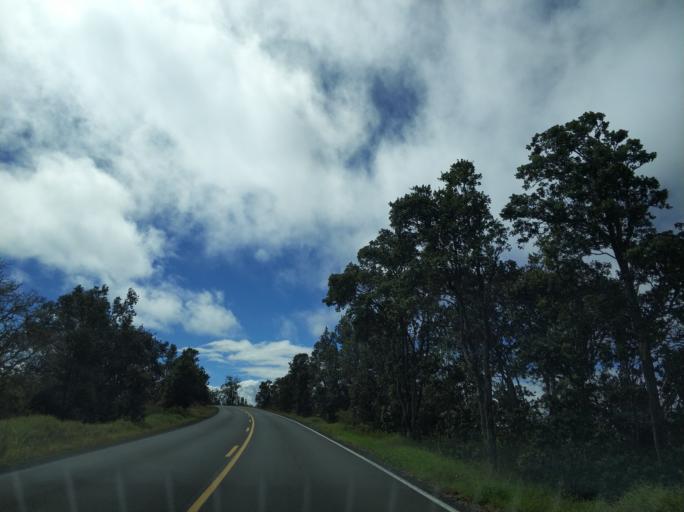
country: US
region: Hawaii
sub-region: Hawaii County
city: Volcano
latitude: 19.4247
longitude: -155.2874
